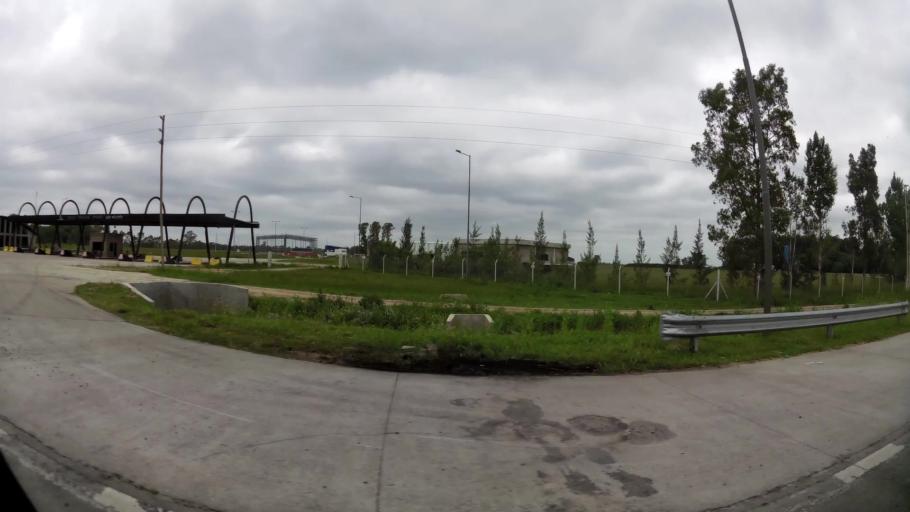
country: AR
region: Buenos Aires
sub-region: Partido de San Vicente
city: San Vicente
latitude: -35.0486
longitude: -58.4259
